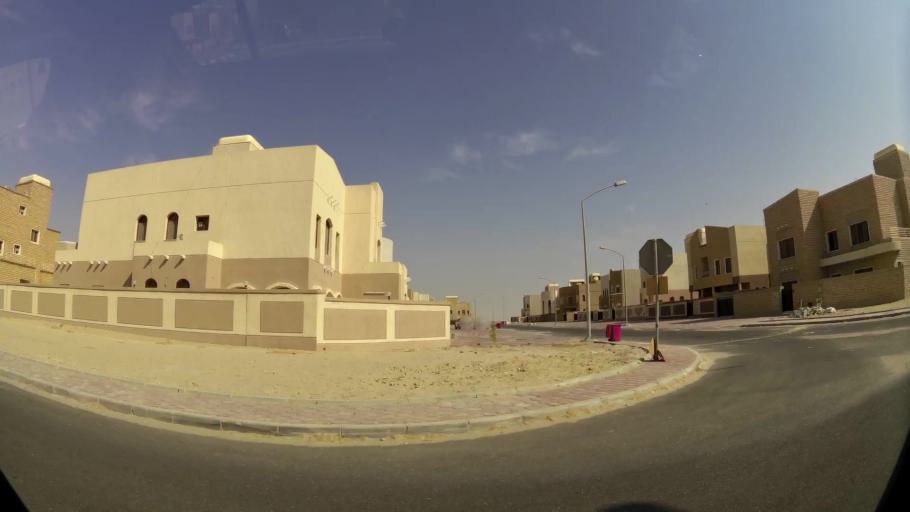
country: KW
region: Al Ahmadi
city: Al Wafrah
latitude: 28.8021
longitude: 48.0715
